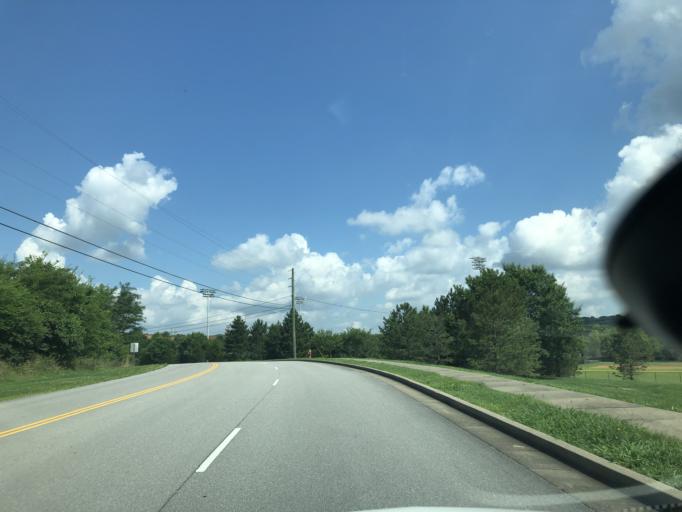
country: US
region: Tennessee
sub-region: Rutherford County
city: La Vergne
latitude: 36.0279
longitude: -86.6174
